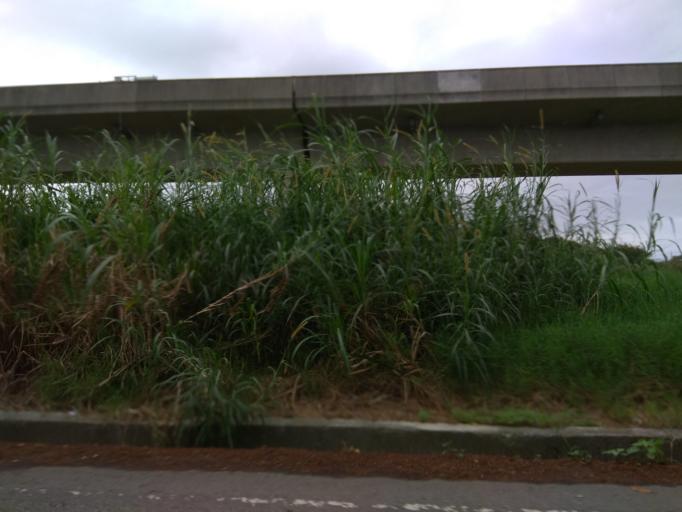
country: TW
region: Taiwan
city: Taoyuan City
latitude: 25.0446
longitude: 121.2152
